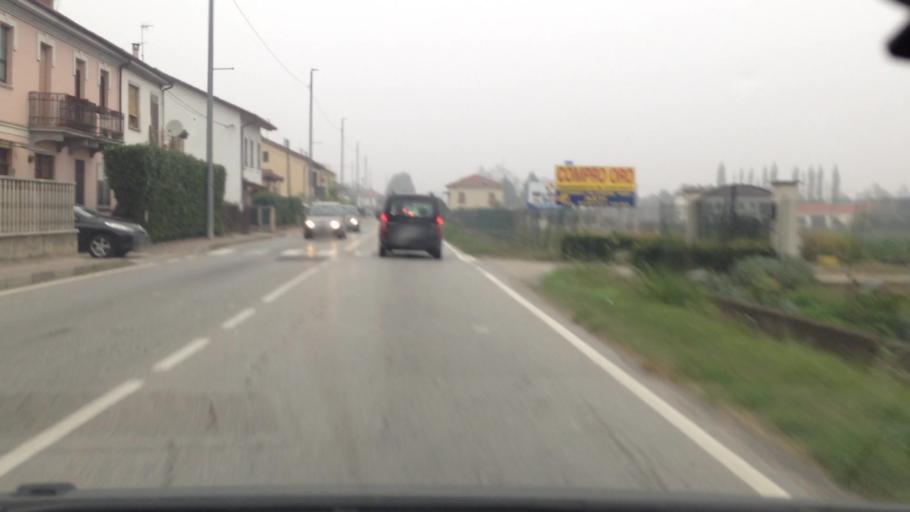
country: IT
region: Piedmont
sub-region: Provincia di Asti
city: Asti
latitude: 44.8804
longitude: 8.2137
